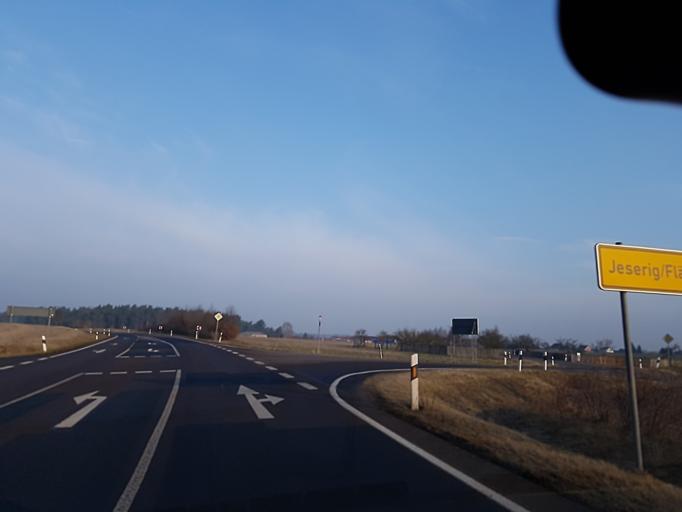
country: DE
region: Brandenburg
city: Wiesenburg
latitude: 52.0798
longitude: 12.4507
